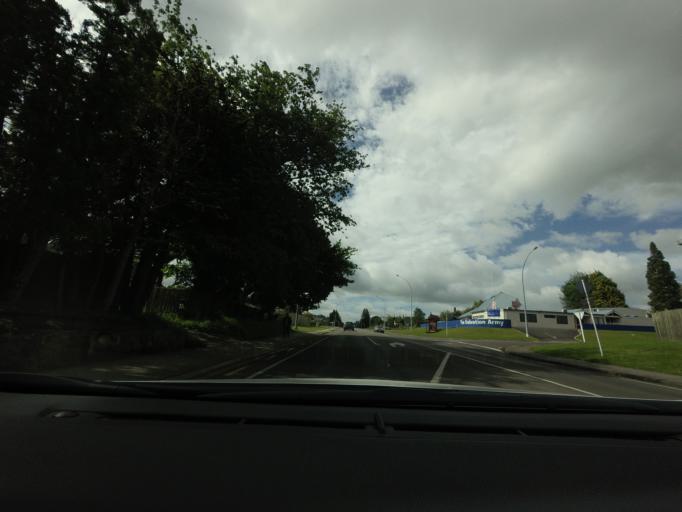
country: NZ
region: Bay of Plenty
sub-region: Rotorua District
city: Rotorua
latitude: -38.1494
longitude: 176.2392
